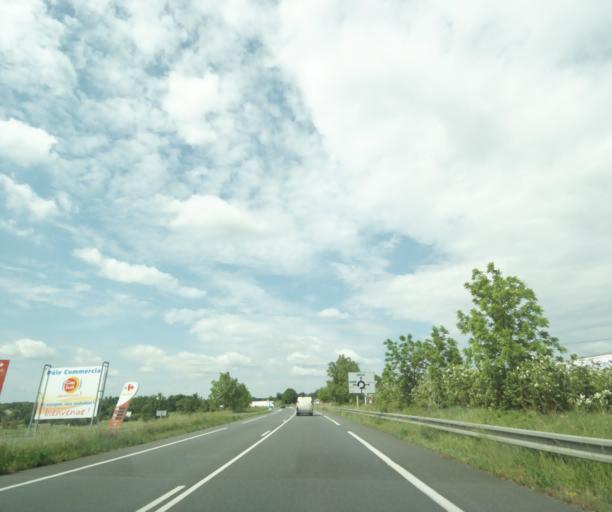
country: FR
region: Pays de la Loire
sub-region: Departement de Maine-et-Loire
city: Distre
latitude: 47.2329
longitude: -0.1125
